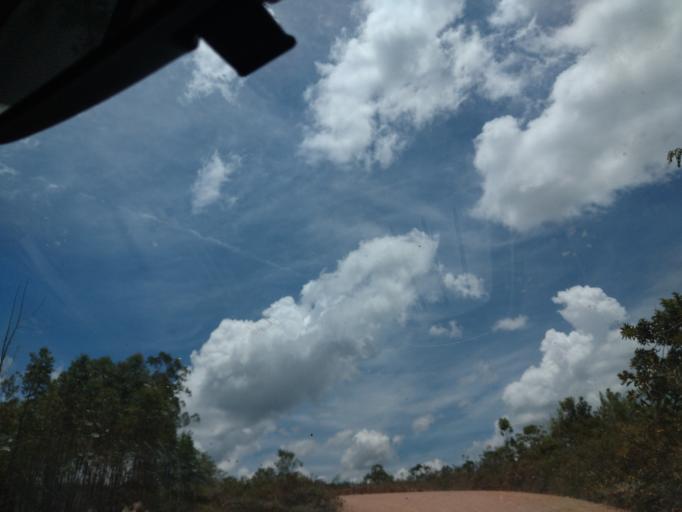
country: BR
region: Minas Gerais
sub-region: Sao Joao Del Rei
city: Sao Joao del Rei
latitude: -20.8973
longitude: -44.3031
